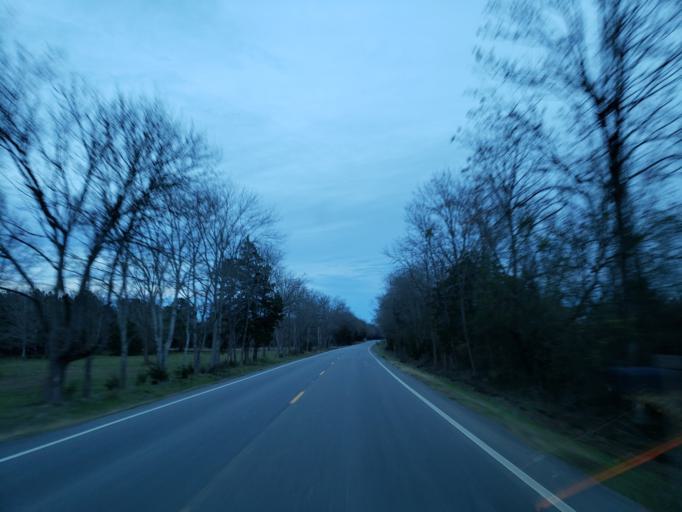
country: US
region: Alabama
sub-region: Sumter County
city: Livingston
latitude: 32.8115
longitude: -88.2488
